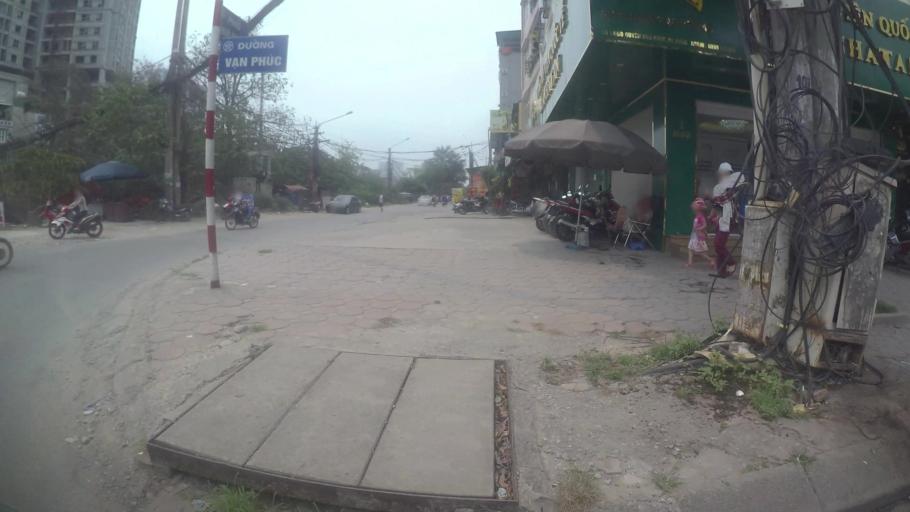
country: VN
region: Ha Noi
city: Ha Dong
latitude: 20.9760
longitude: 105.7765
